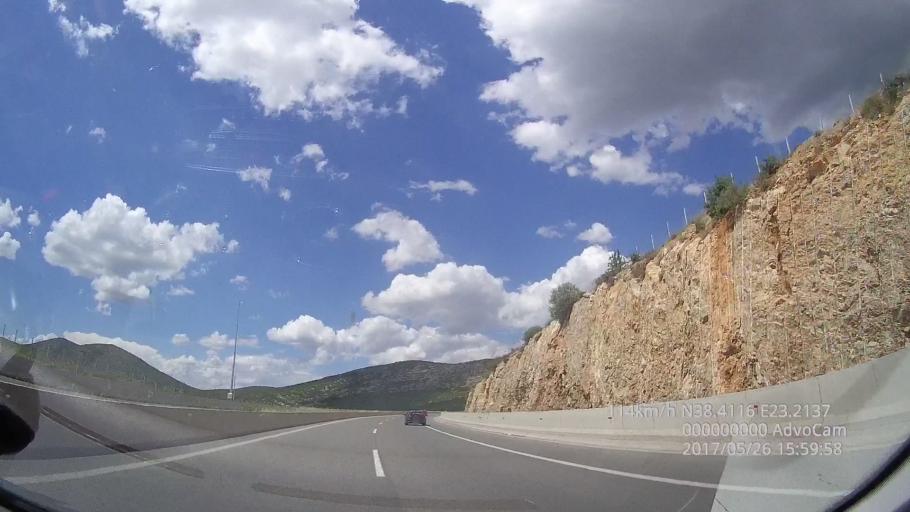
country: GR
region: Central Greece
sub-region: Nomos Fthiotidos
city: Ayios Konstandinos
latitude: 38.7665
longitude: 22.8303
